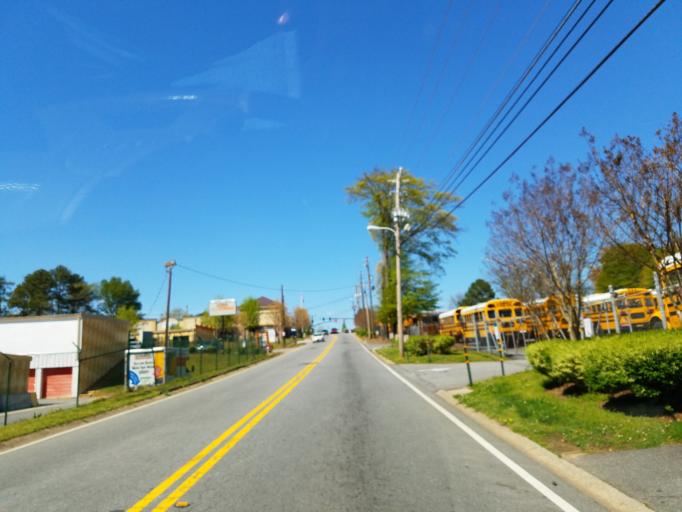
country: US
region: Georgia
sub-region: Cobb County
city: Marietta
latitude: 33.9489
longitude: -84.5238
